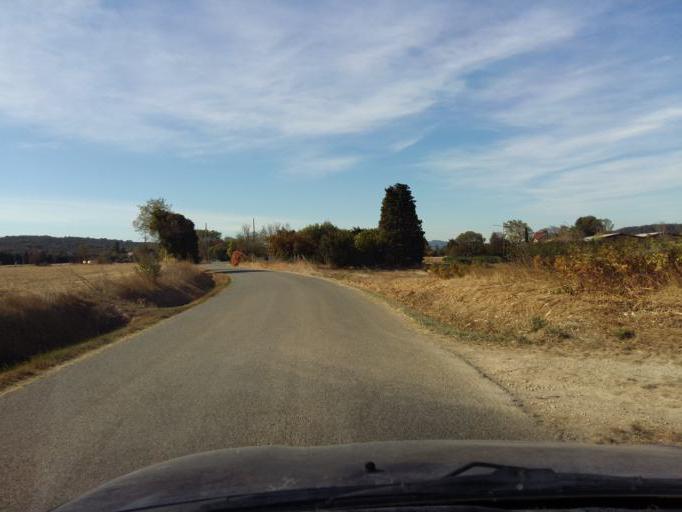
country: FR
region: Provence-Alpes-Cote d'Azur
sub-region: Departement du Vaucluse
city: Piolenc
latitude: 44.1811
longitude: 4.7883
